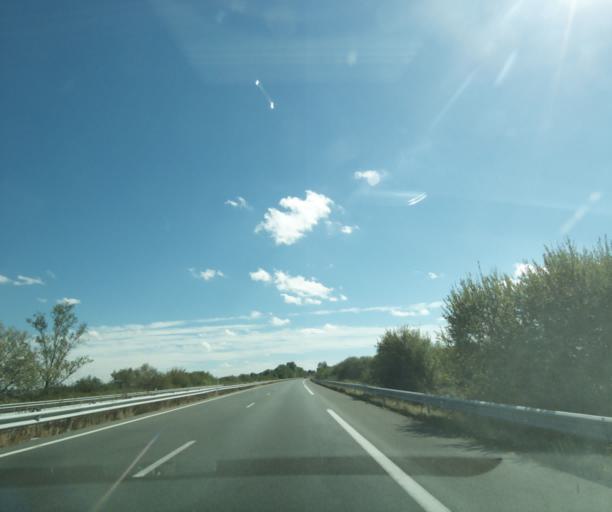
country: FR
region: Aquitaine
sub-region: Departement du Lot-et-Garonne
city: Tonneins
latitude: 44.3692
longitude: 0.2400
